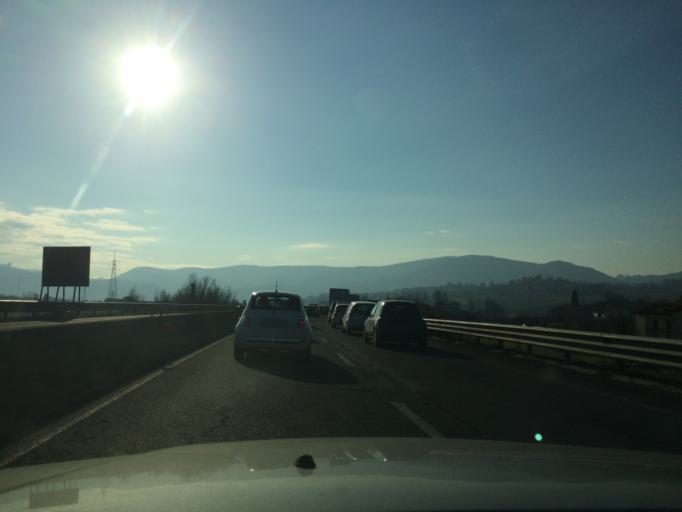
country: IT
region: Umbria
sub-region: Provincia di Terni
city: Narni Scalo
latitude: 42.5536
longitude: 12.5332
